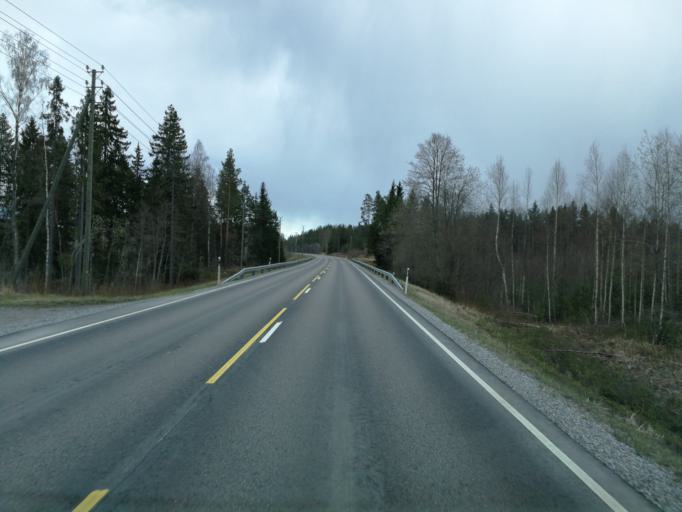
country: FI
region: Uusimaa
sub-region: Raaseporin
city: Inga
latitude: 60.0831
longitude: 23.9468
